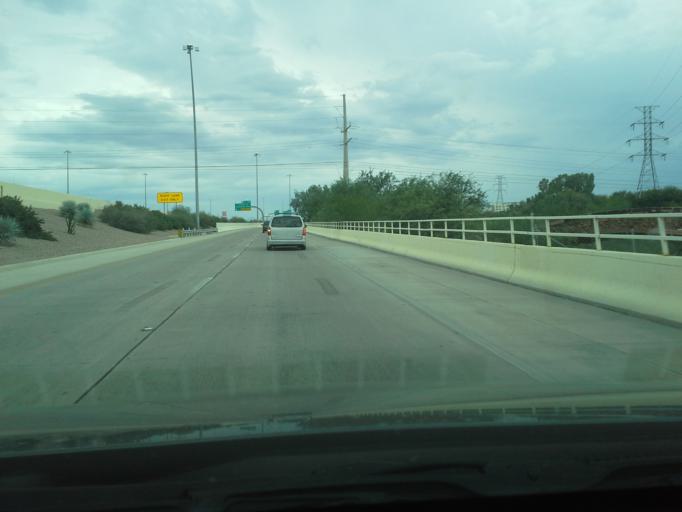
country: US
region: Arizona
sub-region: Pima County
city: South Tucson
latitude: 32.2278
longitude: -110.9823
